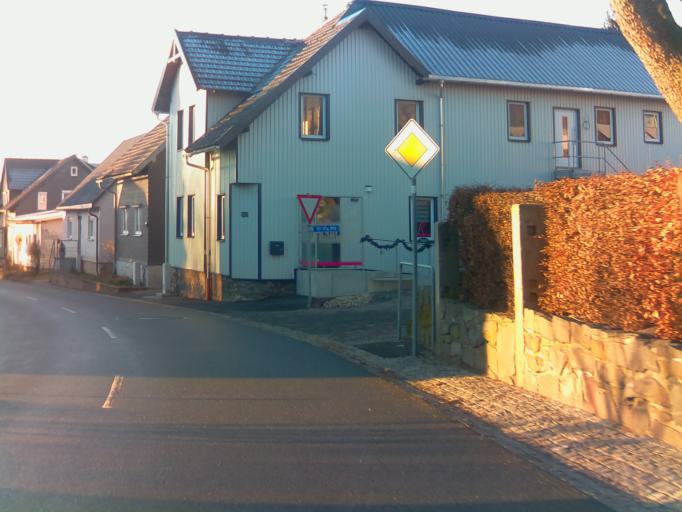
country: DE
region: Thuringia
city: Judenbach
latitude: 50.4015
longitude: 11.2260
